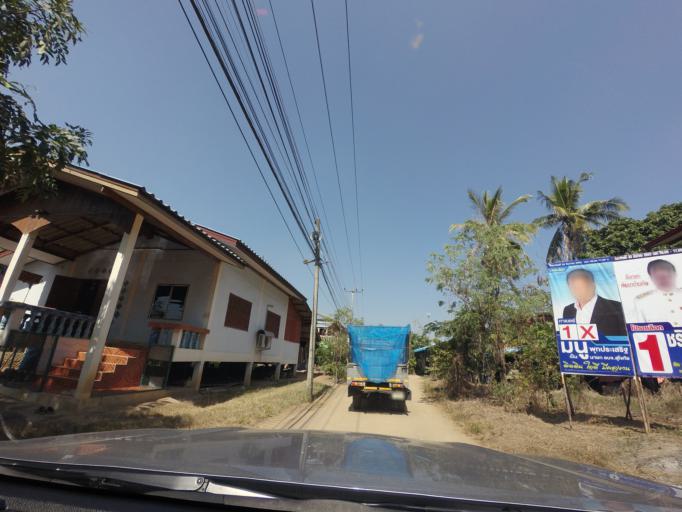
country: TH
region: Sukhothai
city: Si Samrong
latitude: 17.1989
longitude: 99.7726
